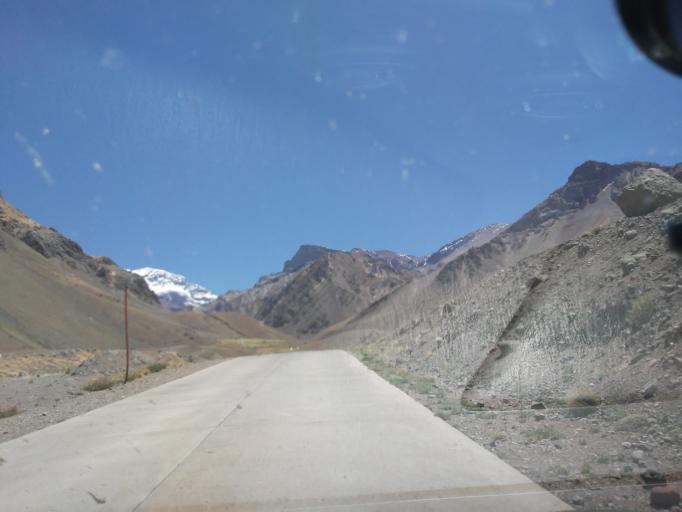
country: CL
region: Valparaiso
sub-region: Provincia de Los Andes
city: Los Andes
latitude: -32.8190
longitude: -69.9422
